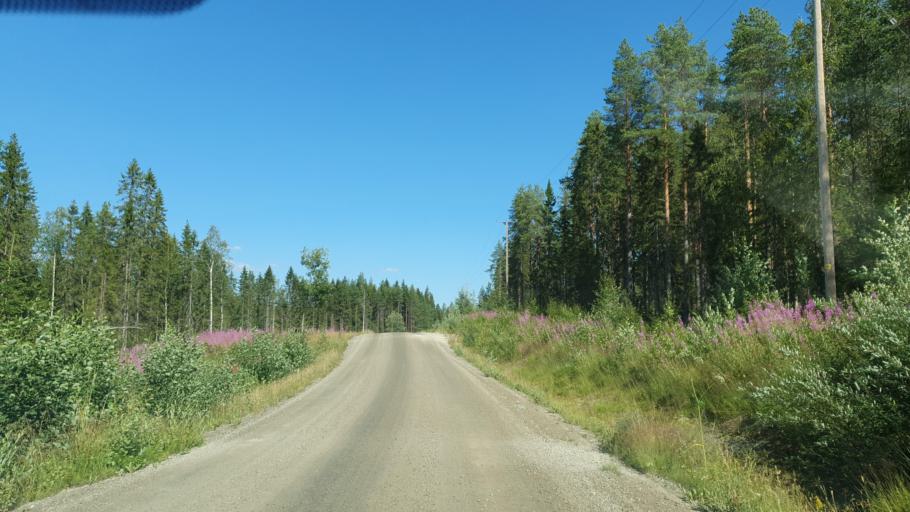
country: FI
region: Kainuu
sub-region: Kehys-Kainuu
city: Kuhmo
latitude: 64.0473
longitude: 29.6290
